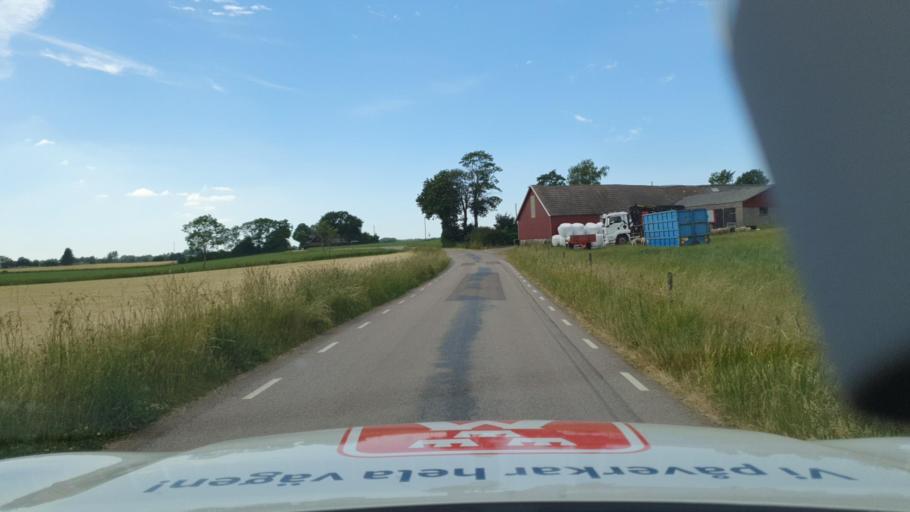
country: SE
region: Skane
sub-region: Sjobo Kommun
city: Sjoebo
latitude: 55.6362
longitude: 13.8054
